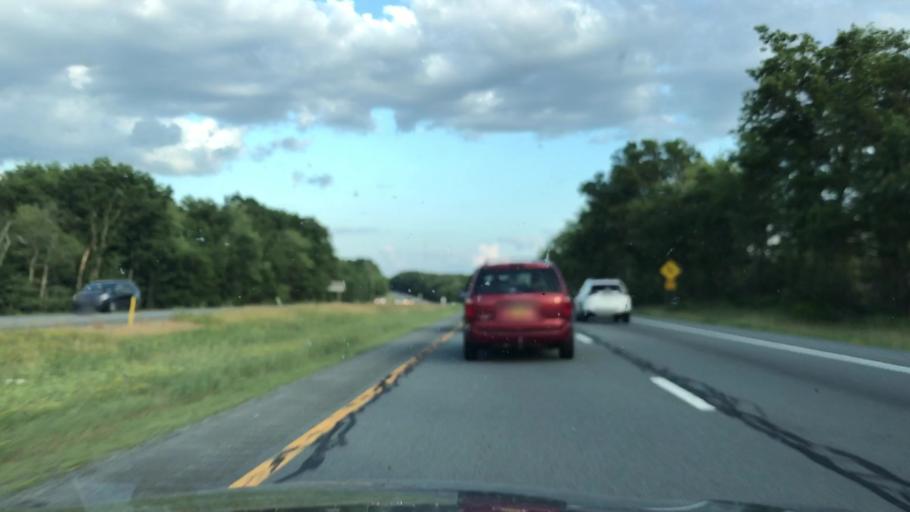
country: US
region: New York
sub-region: Sullivan County
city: Rock Hill
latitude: 41.6084
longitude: -74.5679
